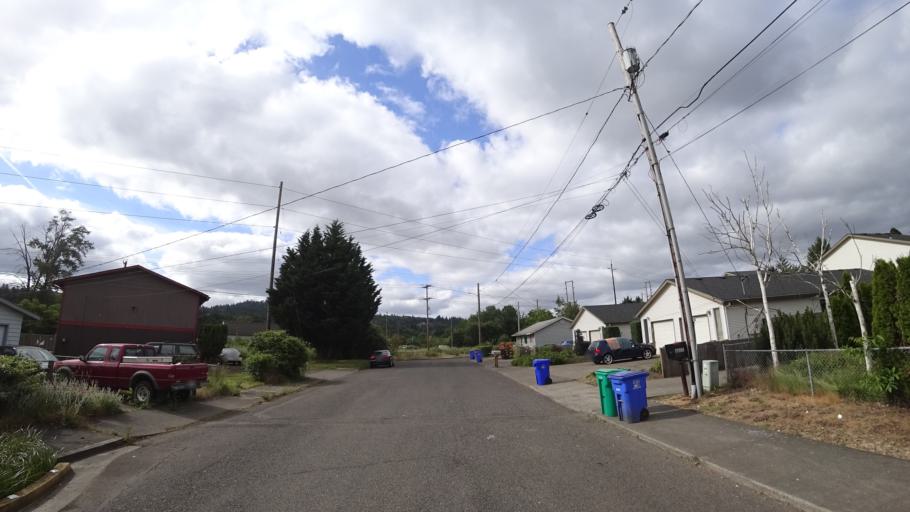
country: US
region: Oregon
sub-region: Multnomah County
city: Lents
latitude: 45.4746
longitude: -122.5635
